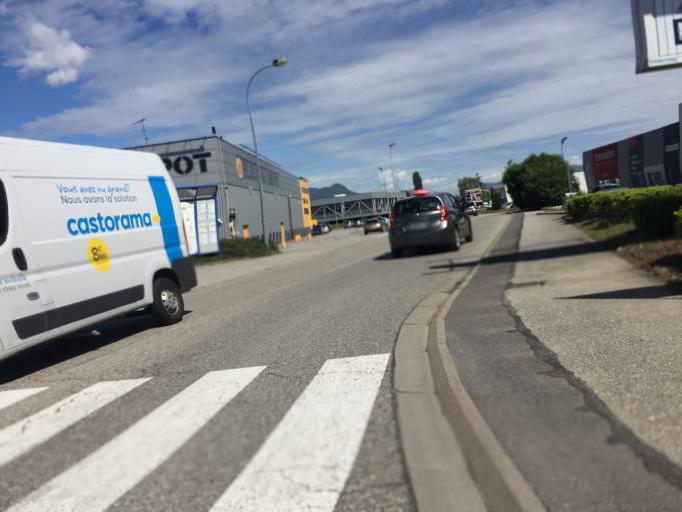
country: FR
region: Rhone-Alpes
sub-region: Departement de la Savoie
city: Voglans
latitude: 45.6151
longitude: 5.8874
